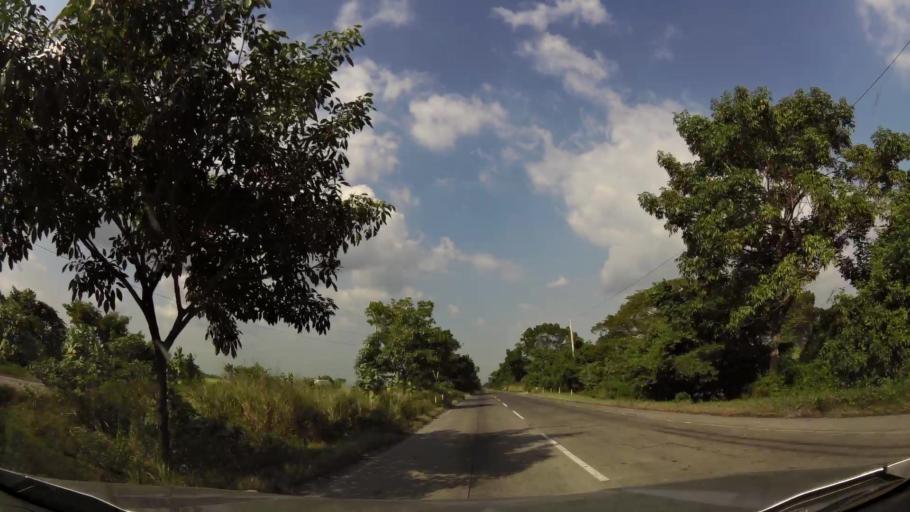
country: GT
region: Escuintla
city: Puerto San Jose
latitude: 14.0251
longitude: -90.7821
